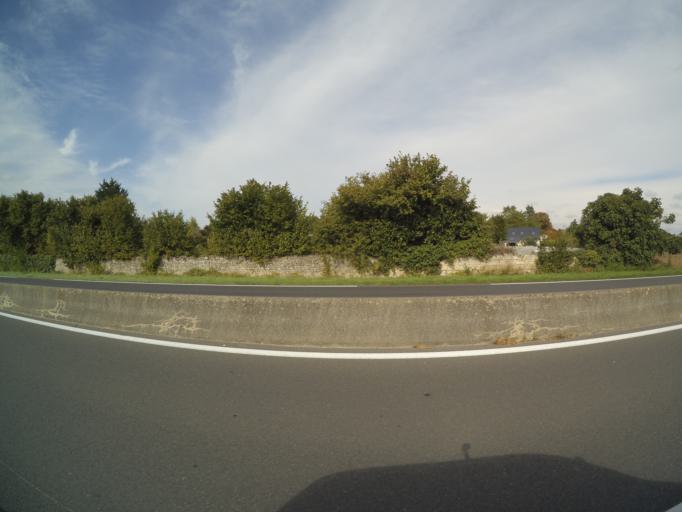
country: FR
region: Pays de la Loire
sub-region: Departement de Maine-et-Loire
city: Distre
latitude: 47.2337
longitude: -0.1167
